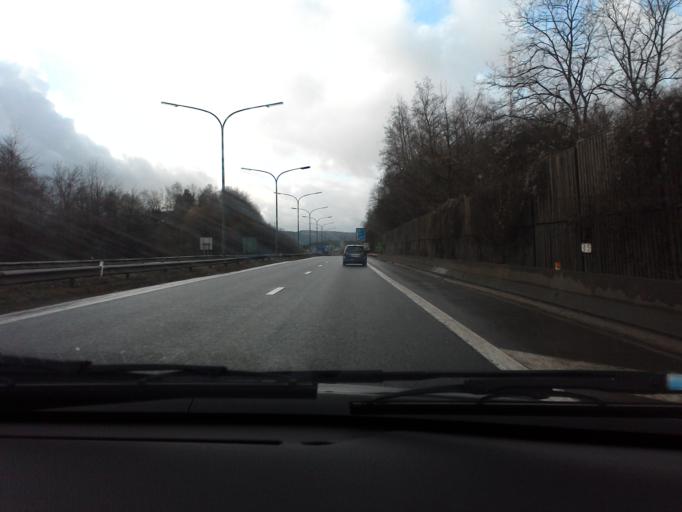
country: BE
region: Wallonia
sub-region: Province de Liege
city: Dison
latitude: 50.6018
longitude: 5.8489
